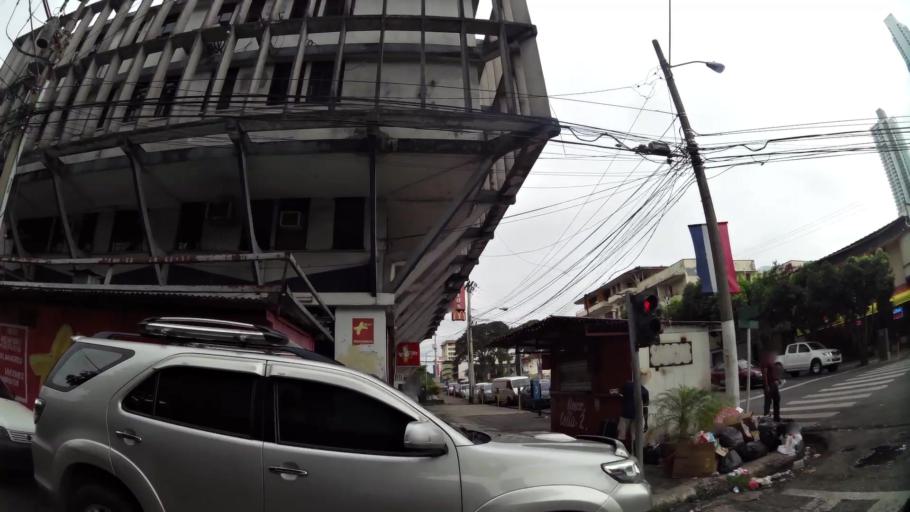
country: PA
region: Panama
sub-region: Distrito de Panama
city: Ancon
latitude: 8.9685
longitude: -79.5366
